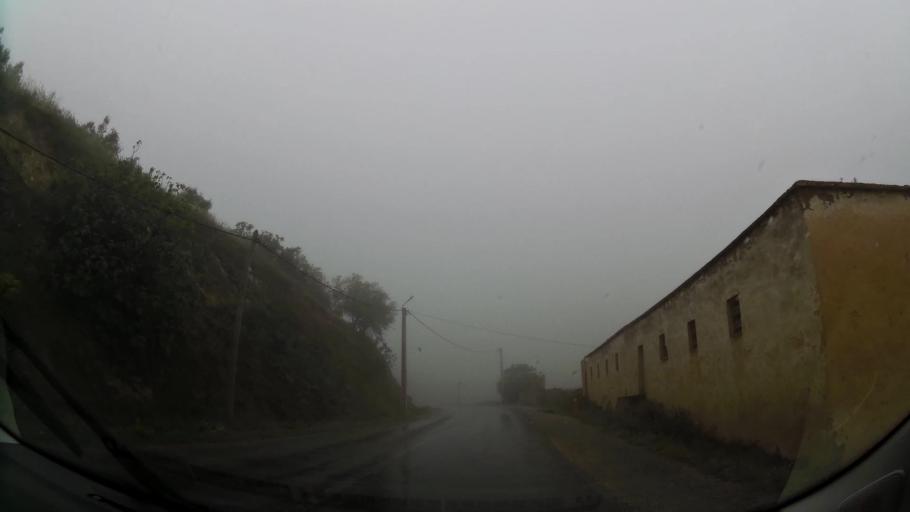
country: MA
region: Oriental
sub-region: Nador
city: Boudinar
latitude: 35.0916
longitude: -3.5321
